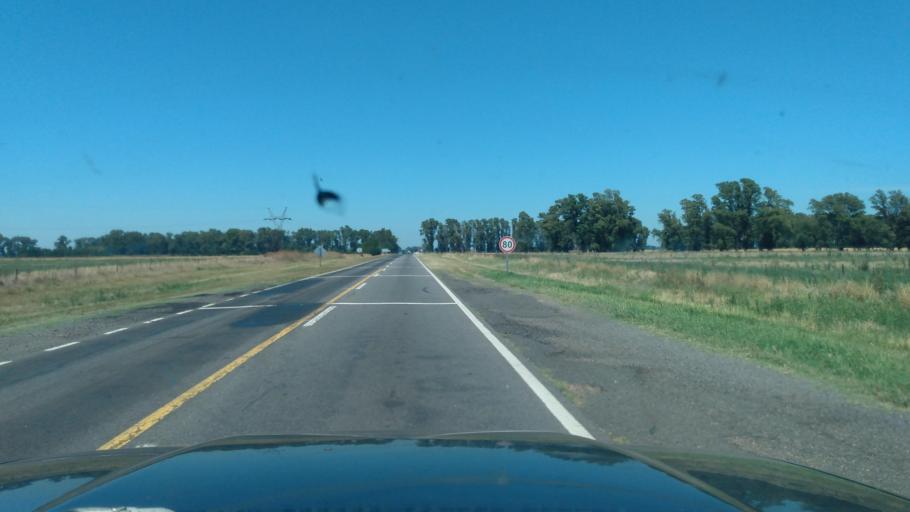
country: AR
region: Buenos Aires
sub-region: Partido de Bragado
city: Bragado
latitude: -35.0924
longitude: -60.3947
